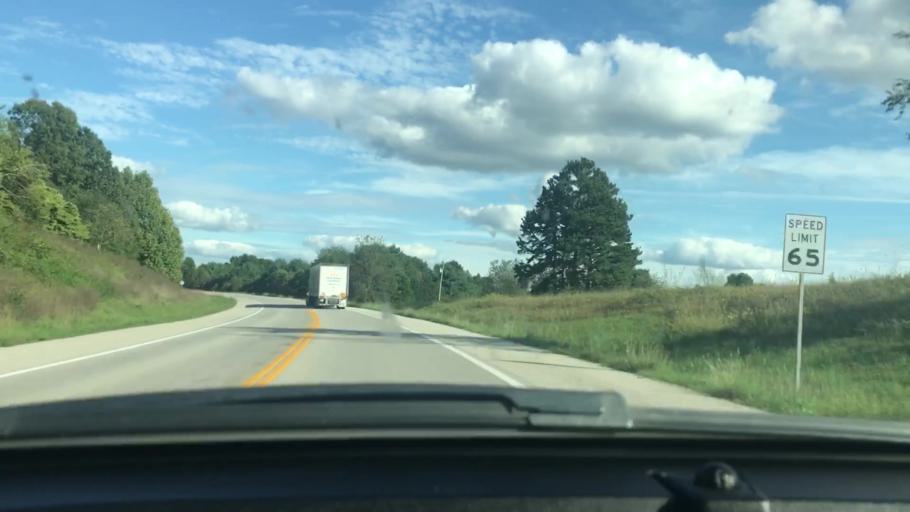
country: US
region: Missouri
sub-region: Oregon County
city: Thayer
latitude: 36.5900
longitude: -91.6414
